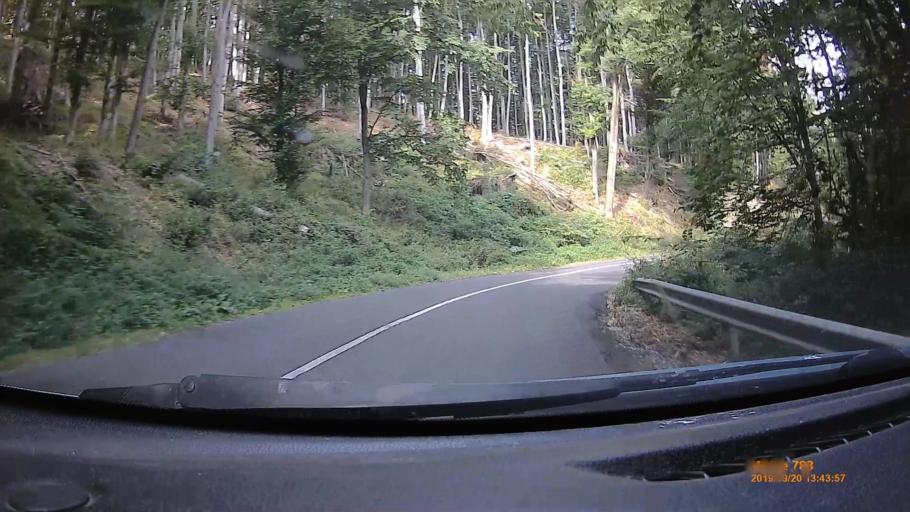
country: HU
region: Borsod-Abauj-Zemplen
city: Saly
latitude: 48.0589
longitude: 20.5579
